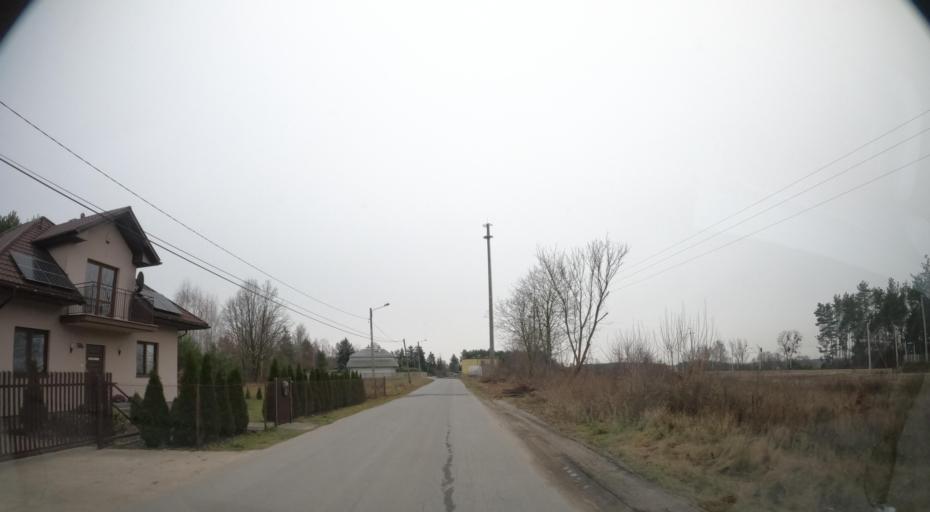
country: PL
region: Masovian Voivodeship
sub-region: Powiat radomski
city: Jastrzebia
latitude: 51.4787
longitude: 21.1947
